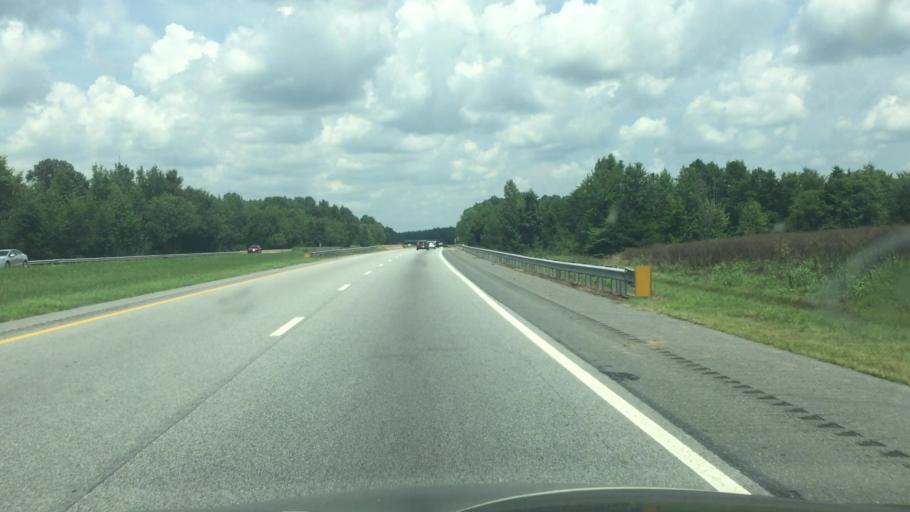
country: US
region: North Carolina
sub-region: Guilford County
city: Pleasant Garden
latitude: 35.9409
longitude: -79.8257
